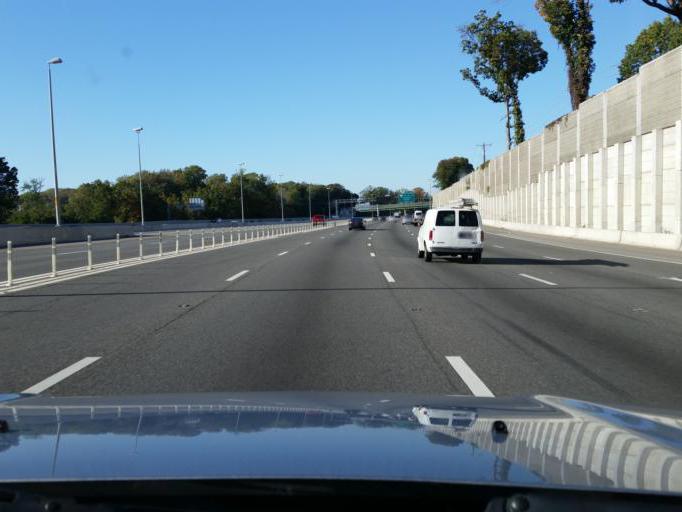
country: US
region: Virginia
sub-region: Fairfax County
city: Ravensworth
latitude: 38.8160
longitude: -77.2208
